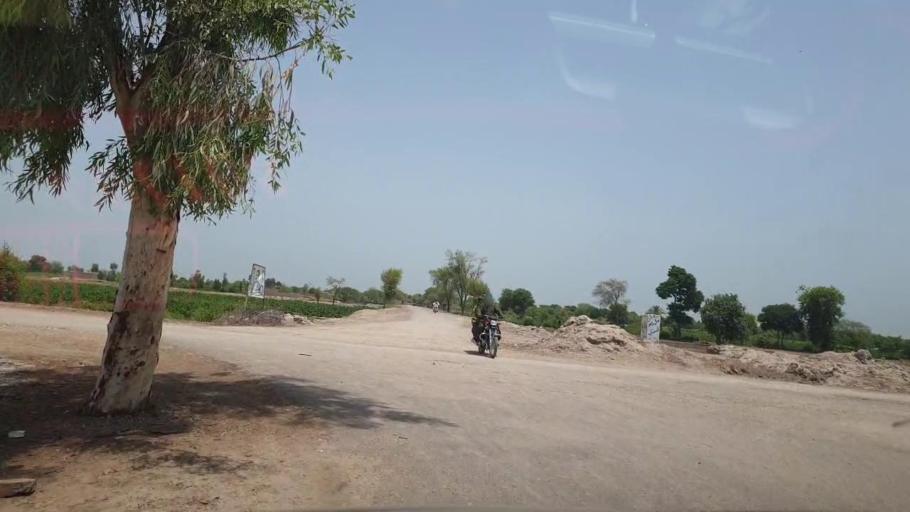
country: PK
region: Sindh
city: Daulatpur
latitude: 26.3895
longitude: 68.1041
